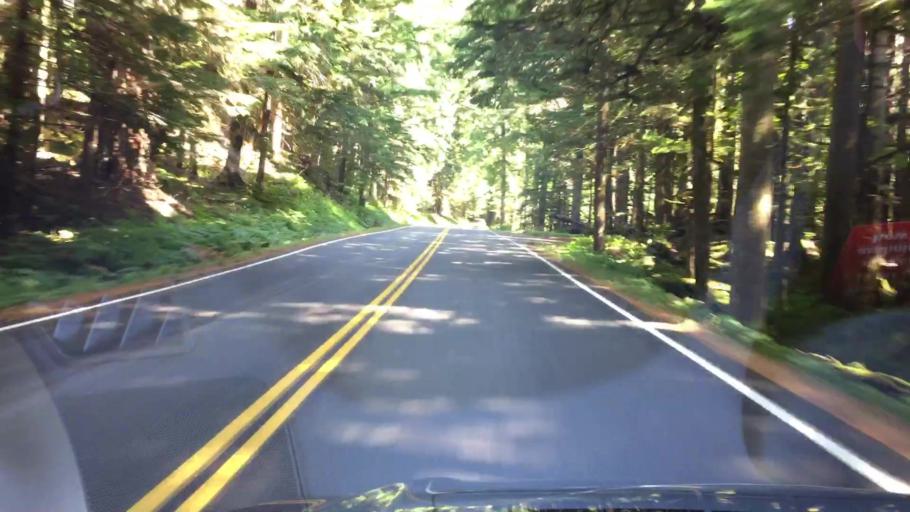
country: US
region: Washington
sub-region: Pierce County
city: Eatonville
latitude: 46.7406
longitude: -121.8847
